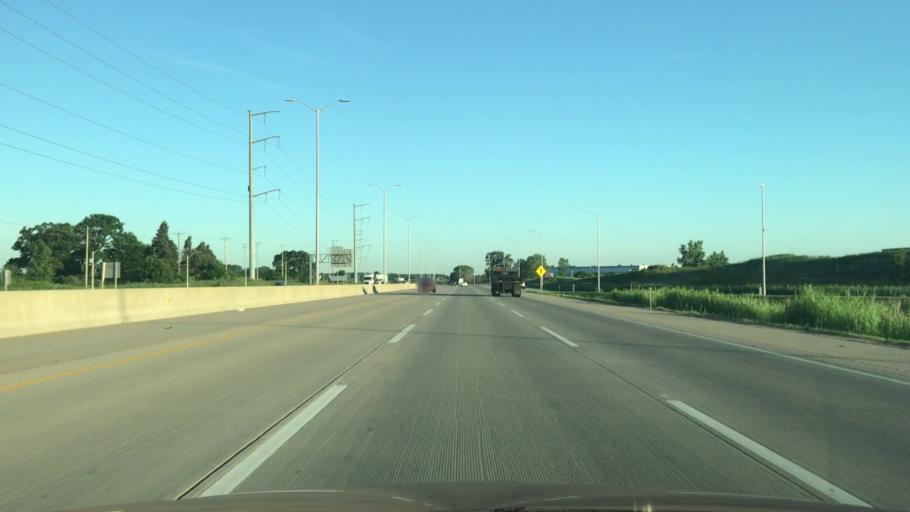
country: US
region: Illinois
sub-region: McHenry County
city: Huntley
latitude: 42.1237
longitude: -88.4354
